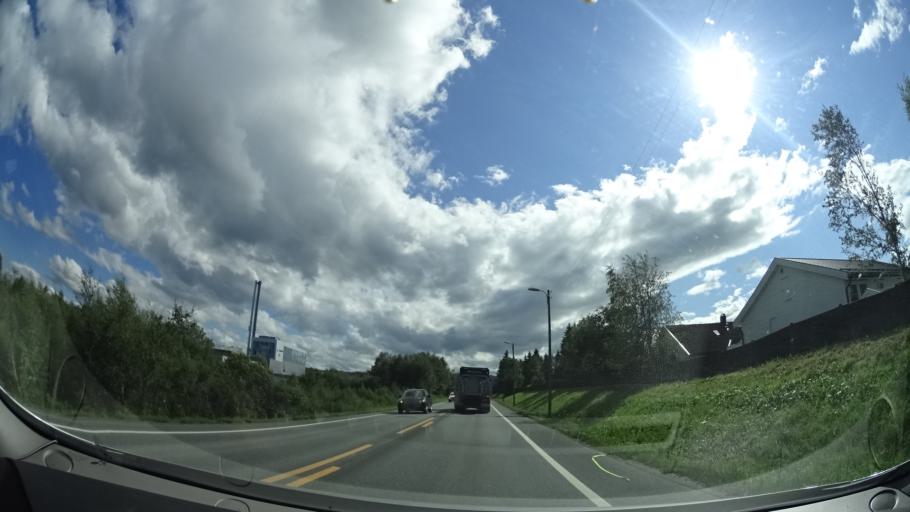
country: NO
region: Sor-Trondelag
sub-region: Trondheim
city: Trondheim
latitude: 63.3511
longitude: 10.3698
